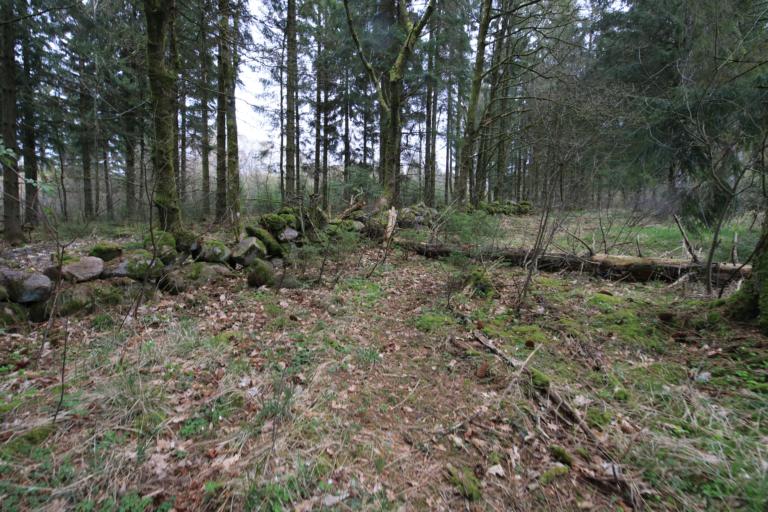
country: SE
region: Halland
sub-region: Varbergs Kommun
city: Tvaaker
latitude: 57.1519
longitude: 12.4543
